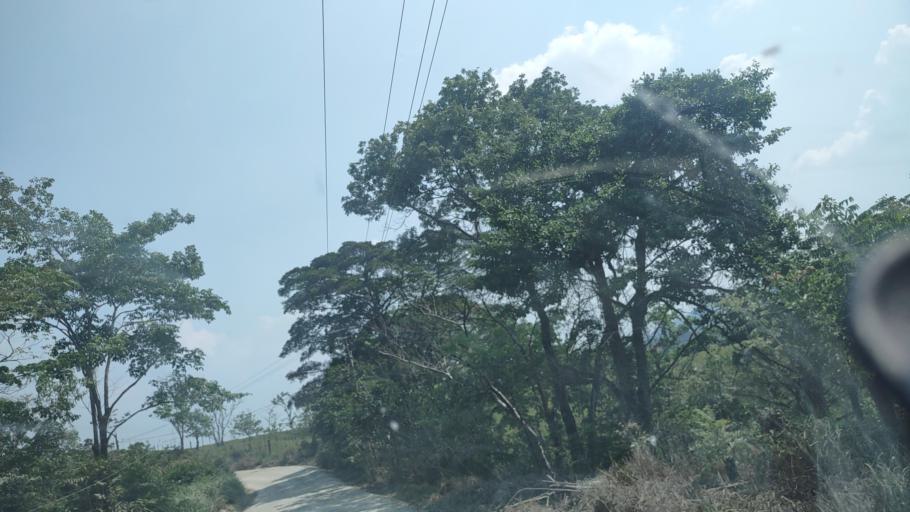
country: MX
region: Tabasco
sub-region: Huimanguillo
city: Francisco Rueda
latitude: 17.5831
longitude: -93.8921
